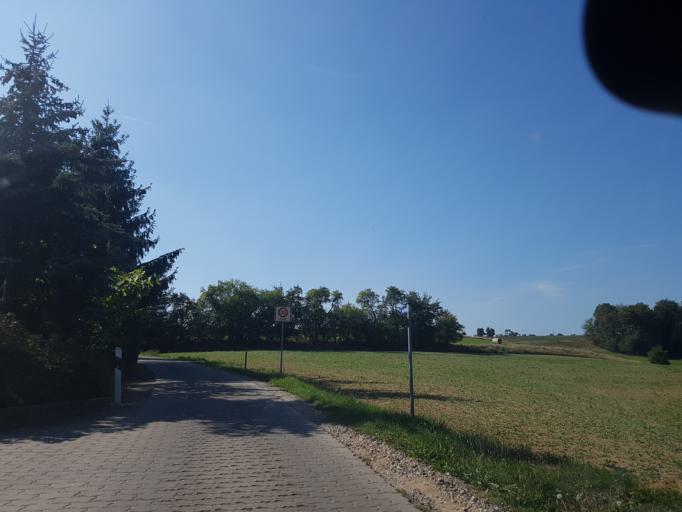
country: DE
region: Saxony
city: Kriebstein
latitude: 51.0461
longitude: 12.9812
